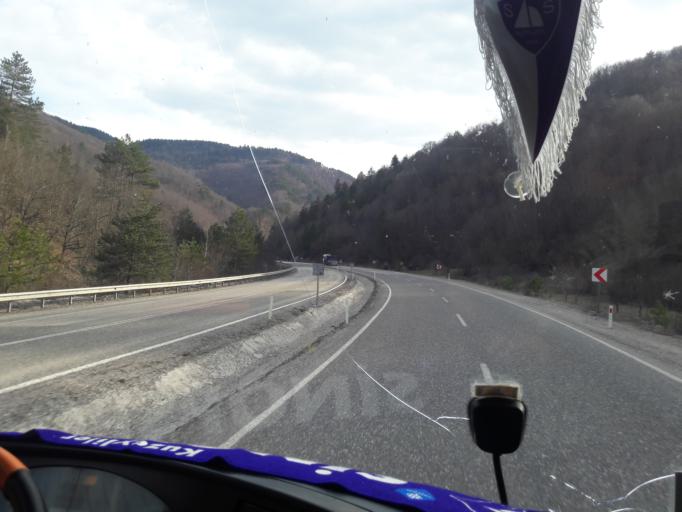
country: TR
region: Kastamonu
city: Kuzyaka
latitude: 41.1412
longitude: 33.7775
